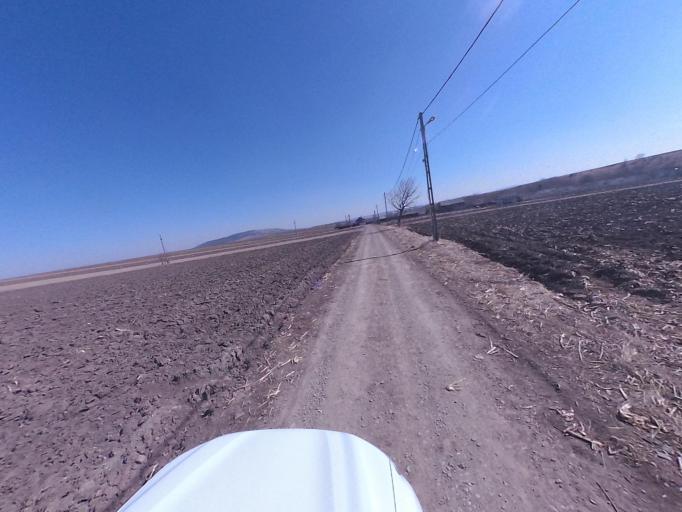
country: RO
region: Neamt
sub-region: Oras Targu Neamt
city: Humulesti
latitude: 47.1852
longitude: 26.3445
